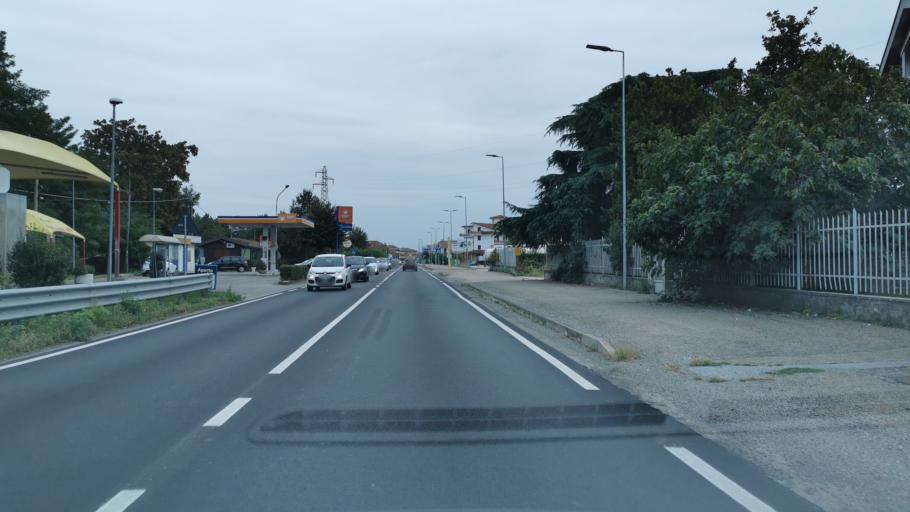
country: IT
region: Piedmont
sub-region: Provincia di Cuneo
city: Roreto
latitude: 44.6761
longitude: 7.8442
